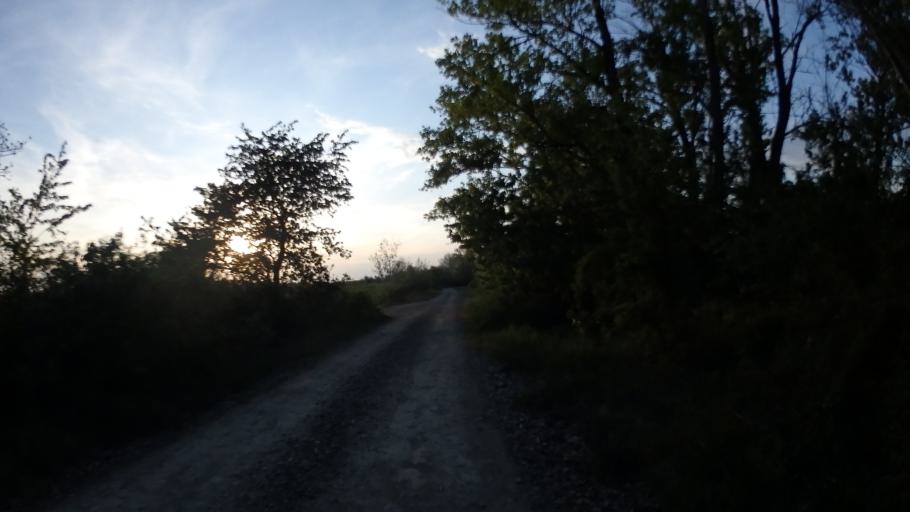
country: CZ
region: South Moravian
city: Ostopovice
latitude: 49.1487
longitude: 16.5492
